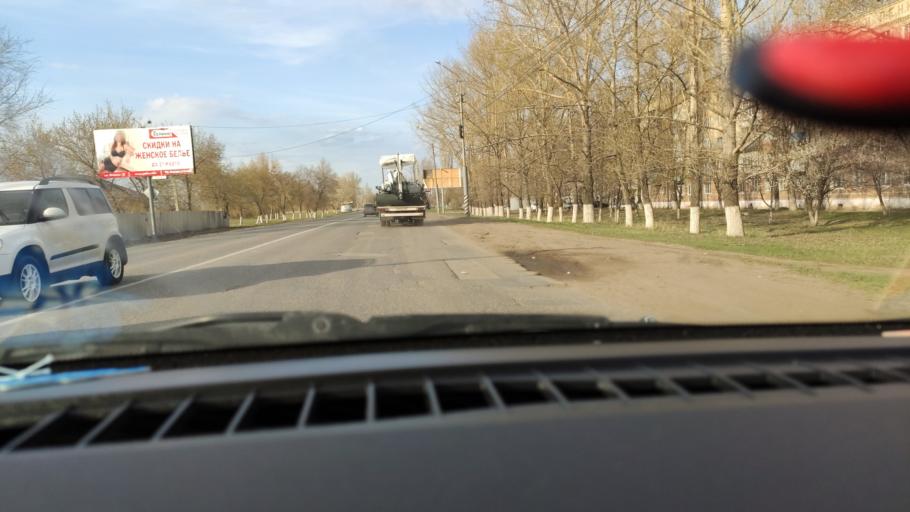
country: RU
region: Saratov
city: Engel's
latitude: 51.4572
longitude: 46.0881
